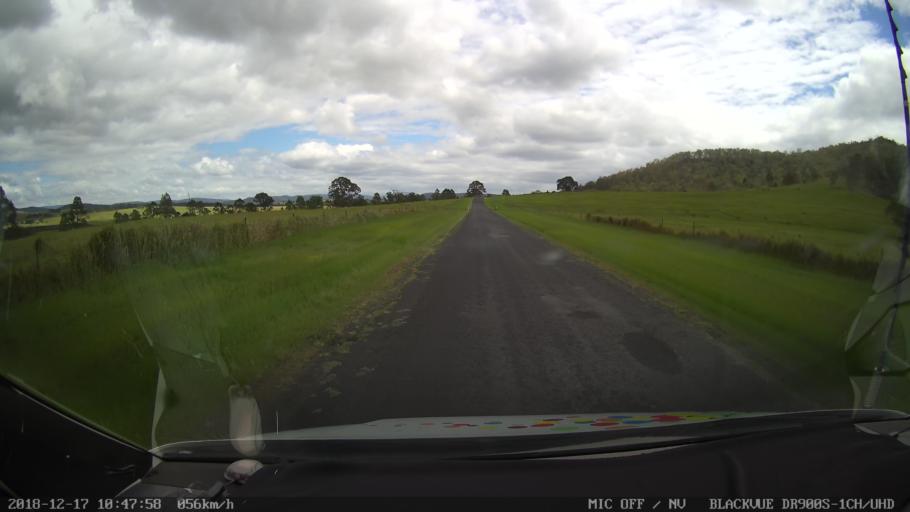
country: AU
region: New South Wales
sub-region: Clarence Valley
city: Gordon
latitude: -28.8769
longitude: 152.5706
